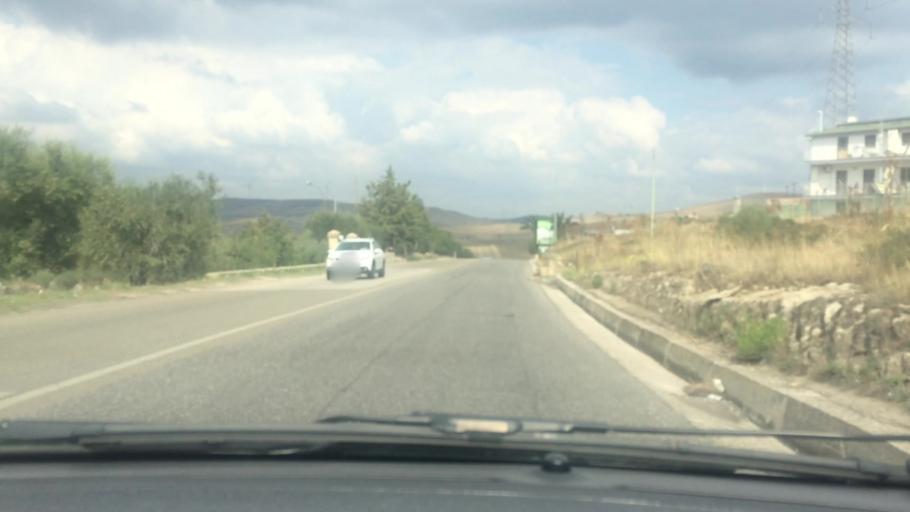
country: IT
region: Basilicate
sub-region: Provincia di Matera
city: Matera
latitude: 40.6854
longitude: 16.5702
